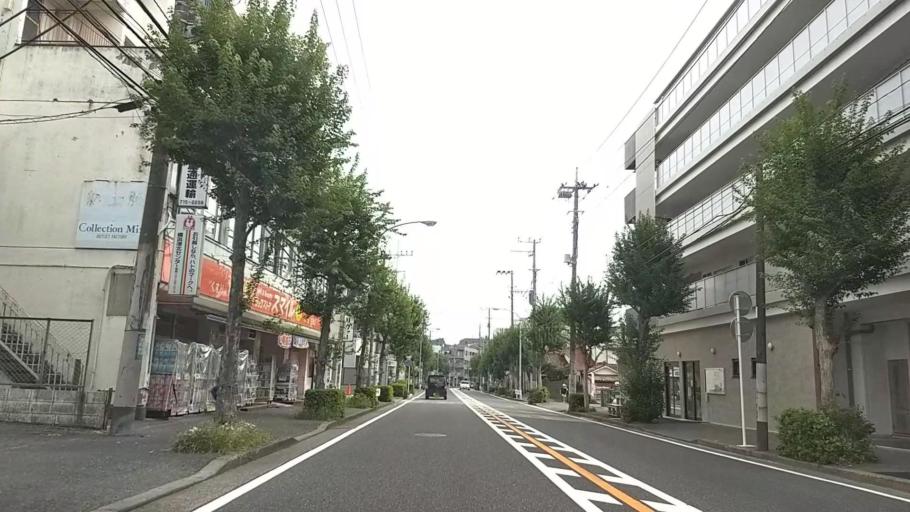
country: JP
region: Kanagawa
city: Yokohama
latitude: 35.4241
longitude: 139.5896
